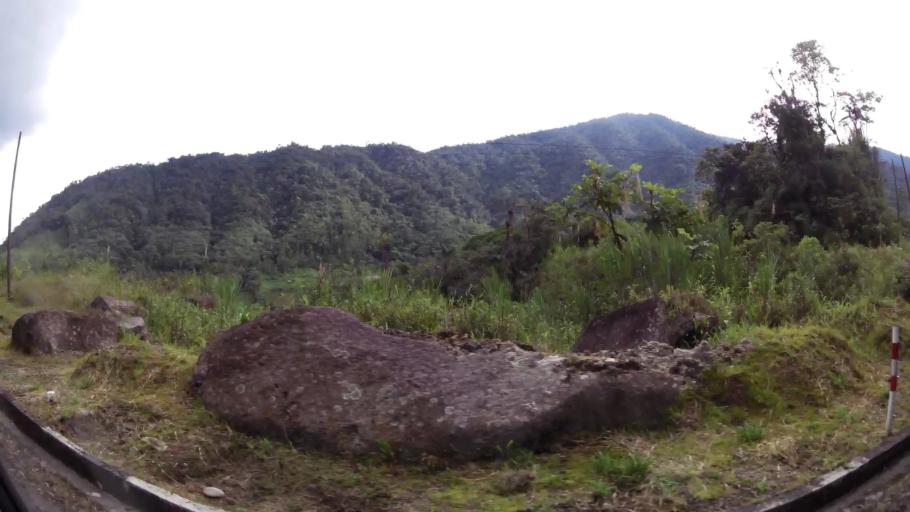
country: EC
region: Pastaza
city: Puyo
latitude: -1.4505
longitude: -78.1526
